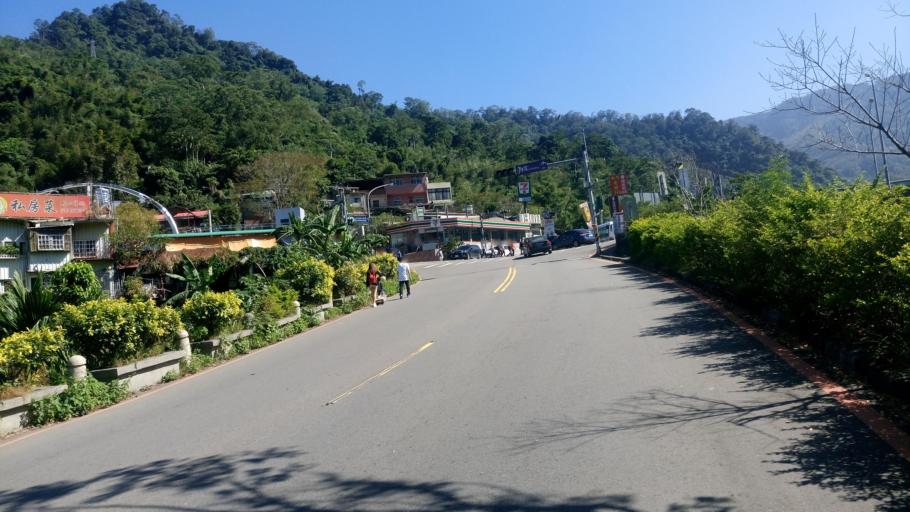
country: TW
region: Taiwan
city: Daxi
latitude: 24.7036
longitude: 121.1826
